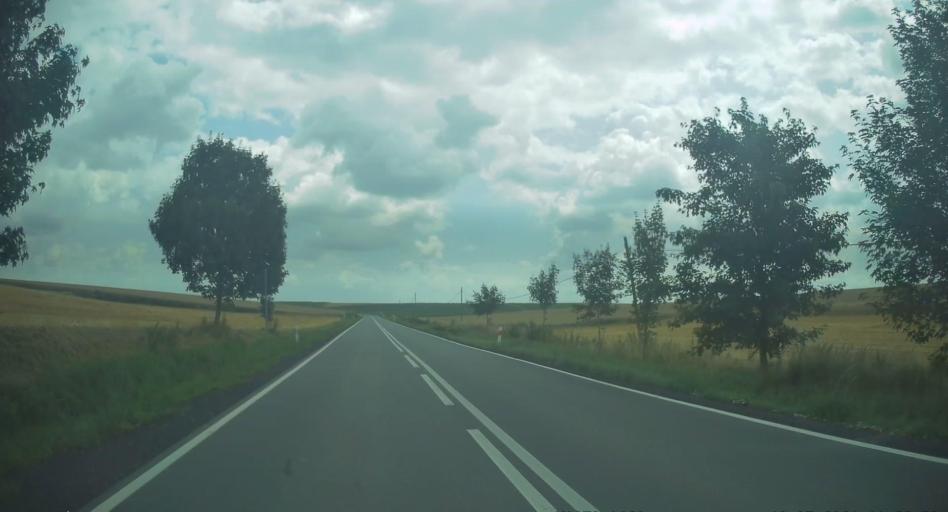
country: PL
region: Opole Voivodeship
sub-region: Powiat prudnicki
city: Raclawice Slaskie
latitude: 50.3523
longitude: 17.8065
